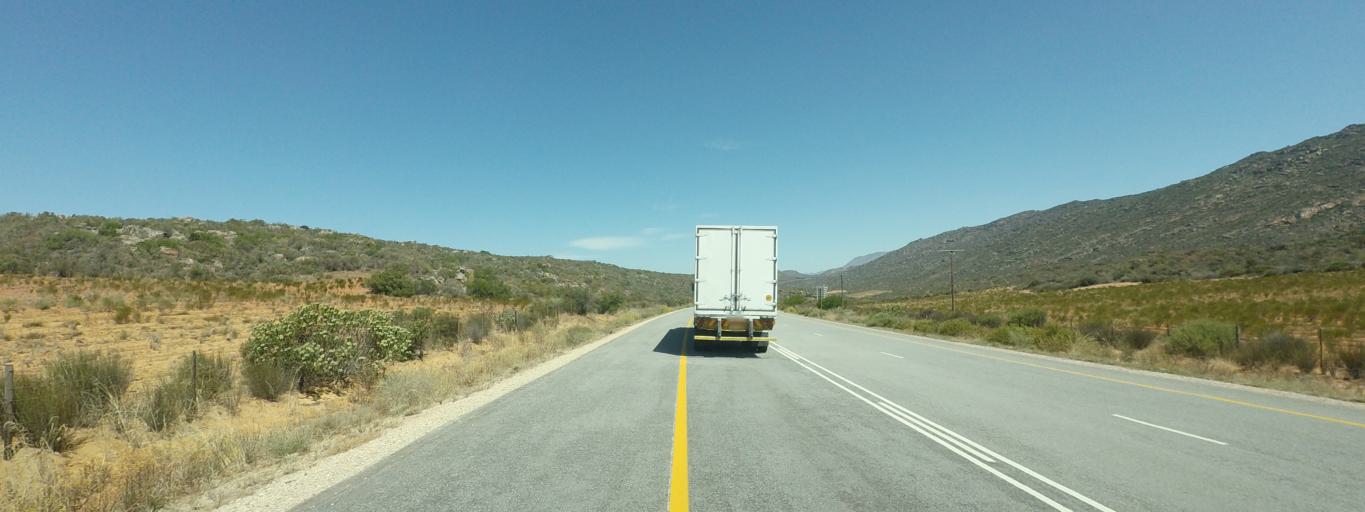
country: ZA
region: Western Cape
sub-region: West Coast District Municipality
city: Clanwilliam
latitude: -32.3298
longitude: 18.9239
